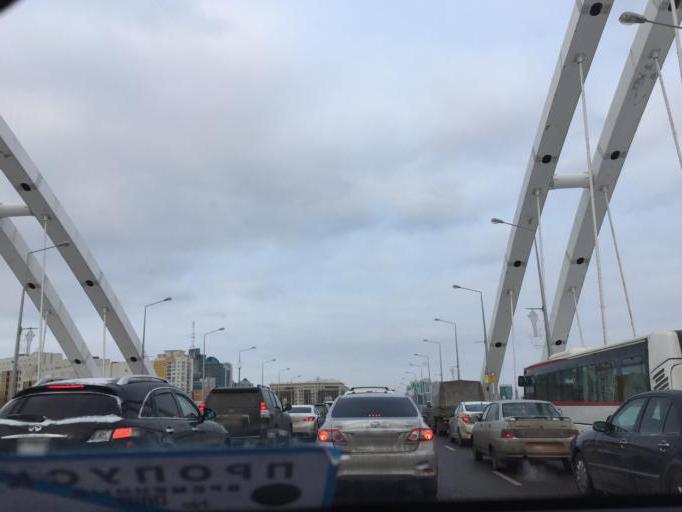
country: KZ
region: Astana Qalasy
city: Astana
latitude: 51.1313
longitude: 71.4472
